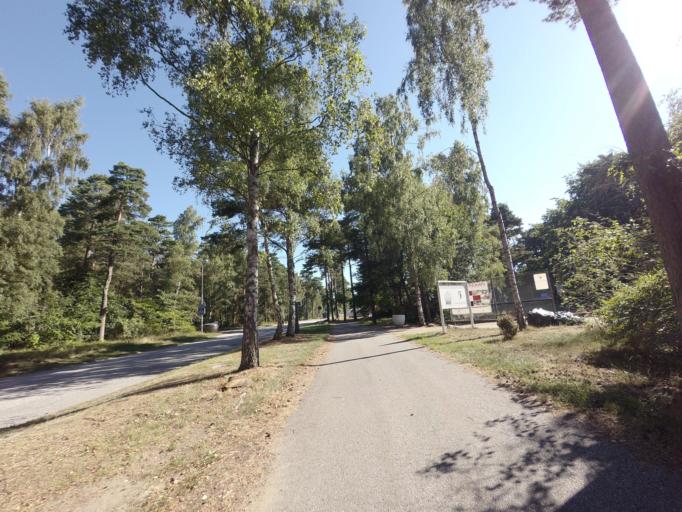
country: SE
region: Skane
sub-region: Ystads Kommun
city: Ystad
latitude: 55.4246
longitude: 13.8462
